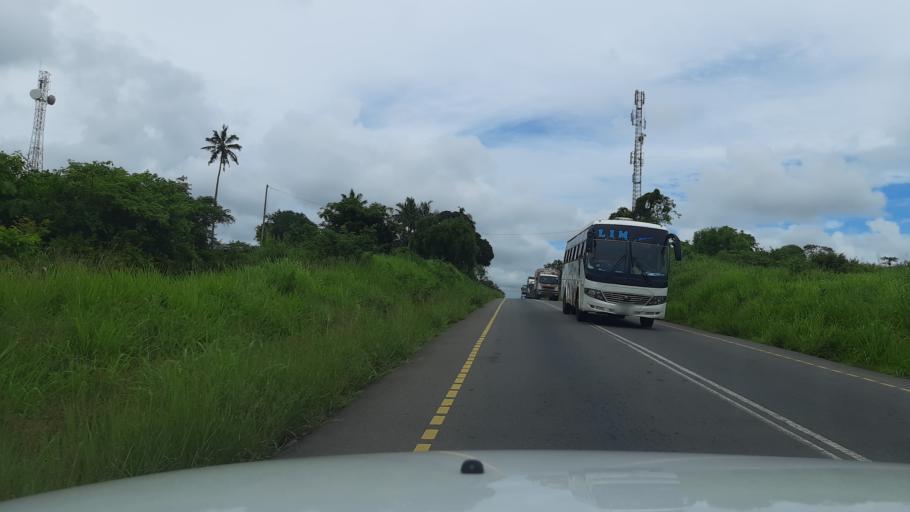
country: TZ
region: Pwani
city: Lugoba
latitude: -6.0274
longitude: 38.2355
